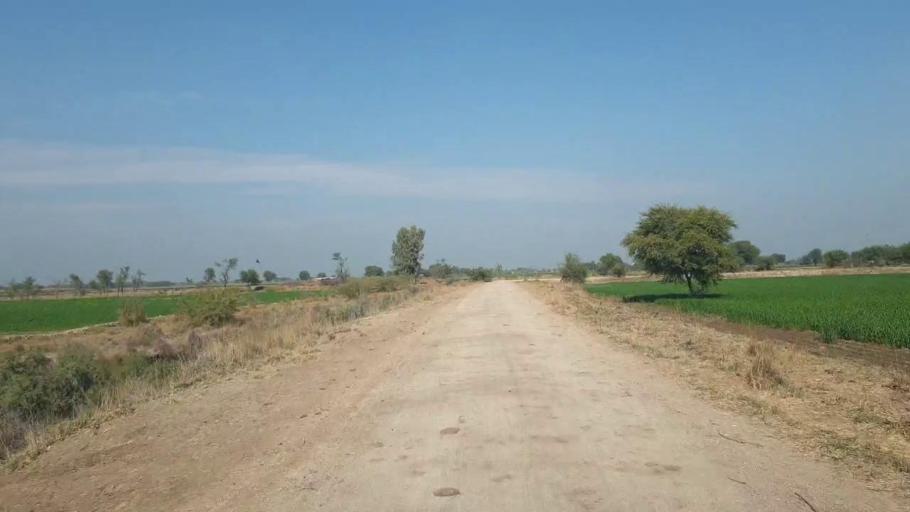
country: PK
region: Sindh
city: Shahdadpur
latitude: 25.9841
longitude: 68.5144
